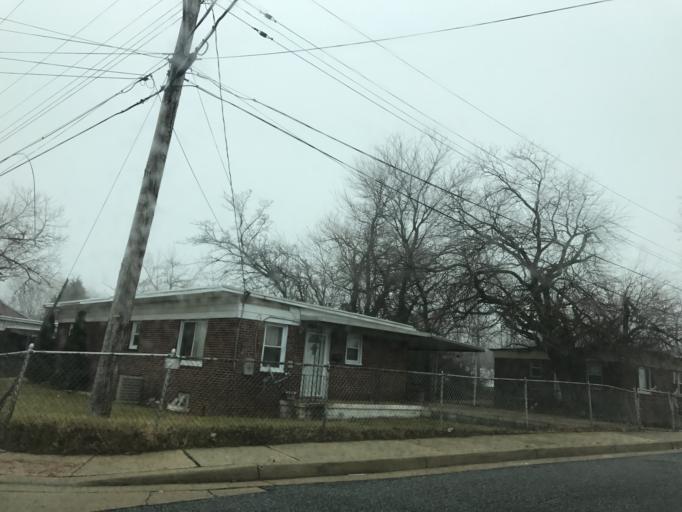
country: US
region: Maryland
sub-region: Baltimore County
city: Dundalk
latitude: 39.2352
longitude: -76.5048
